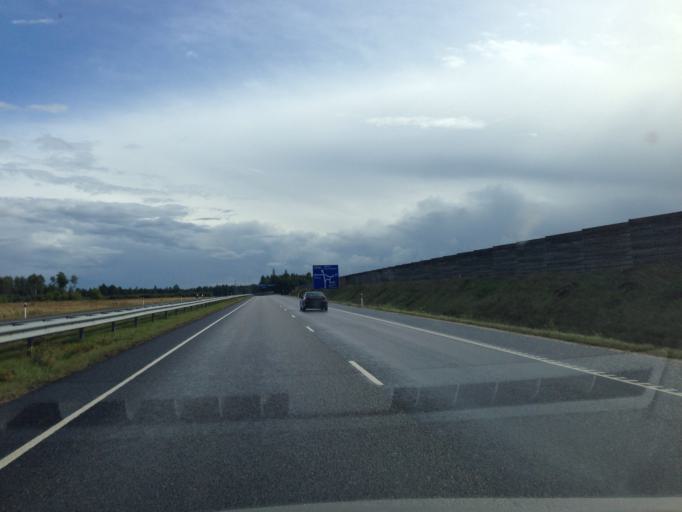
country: EE
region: Jaervamaa
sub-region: Paide linn
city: Paide
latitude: 58.9076
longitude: 25.6289
